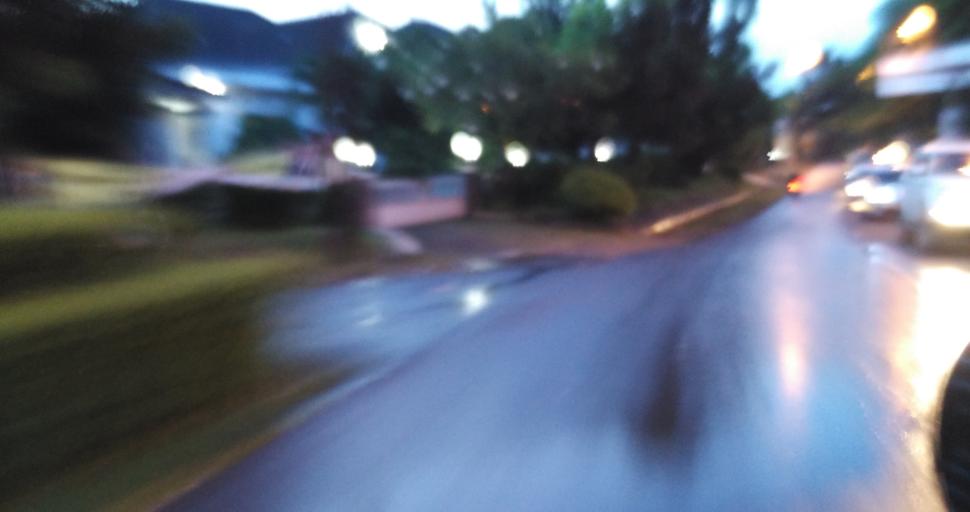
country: ID
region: Central Java
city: Semarang
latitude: -7.0058
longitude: 110.4171
